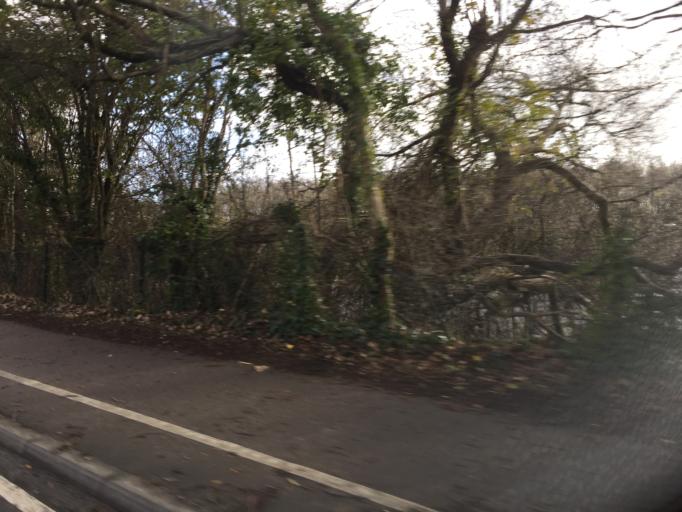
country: GB
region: England
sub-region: Hampshire
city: Chandlers Ford
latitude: 50.9963
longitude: -1.3617
